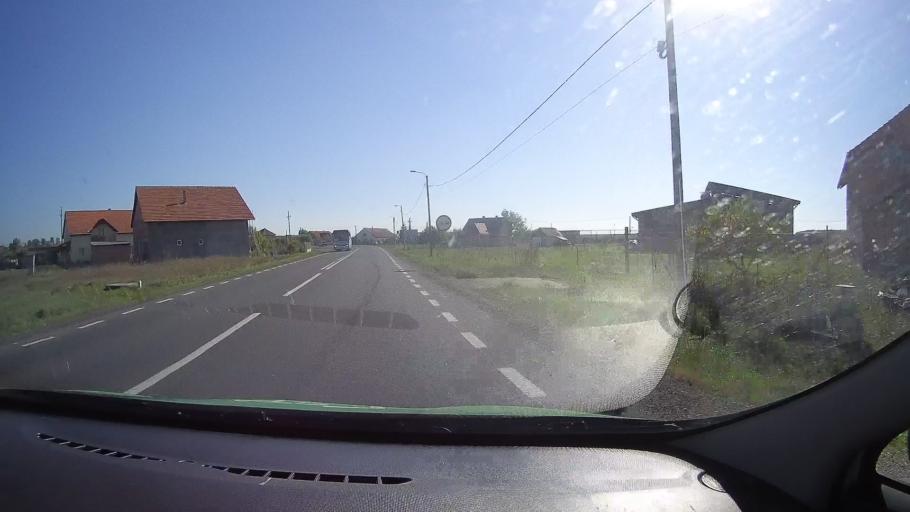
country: RO
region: Satu Mare
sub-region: Oras Ardud
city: Ardud
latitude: 47.6545
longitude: 22.8852
